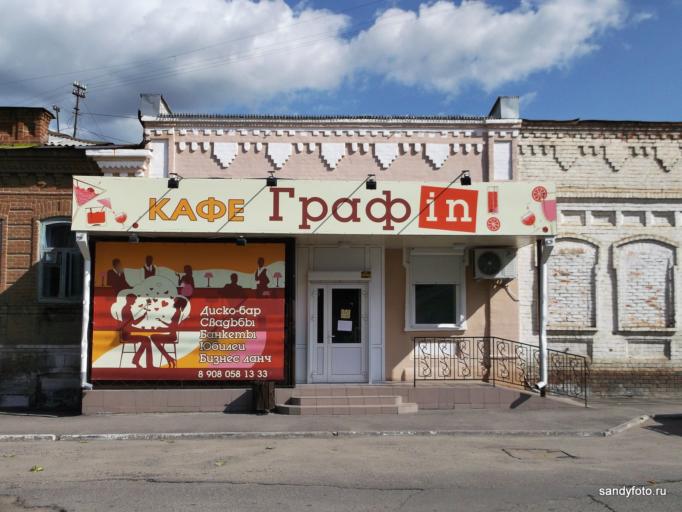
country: RU
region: Chelyabinsk
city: Troitsk
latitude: 54.0854
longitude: 61.5556
